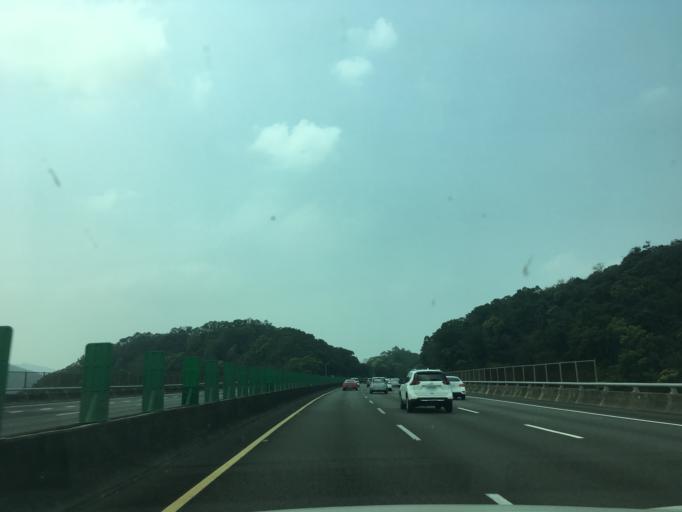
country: TW
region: Taiwan
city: Daxi
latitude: 24.7973
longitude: 121.1846
